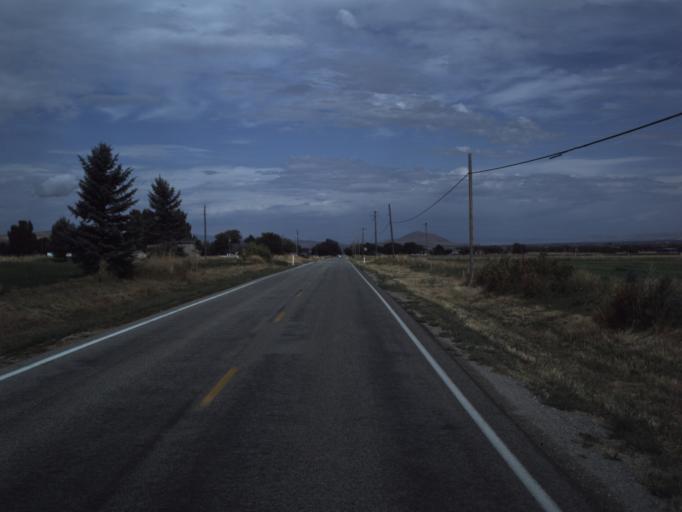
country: US
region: Utah
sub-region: Cache County
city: Mendon
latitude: 41.7215
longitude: -111.9791
